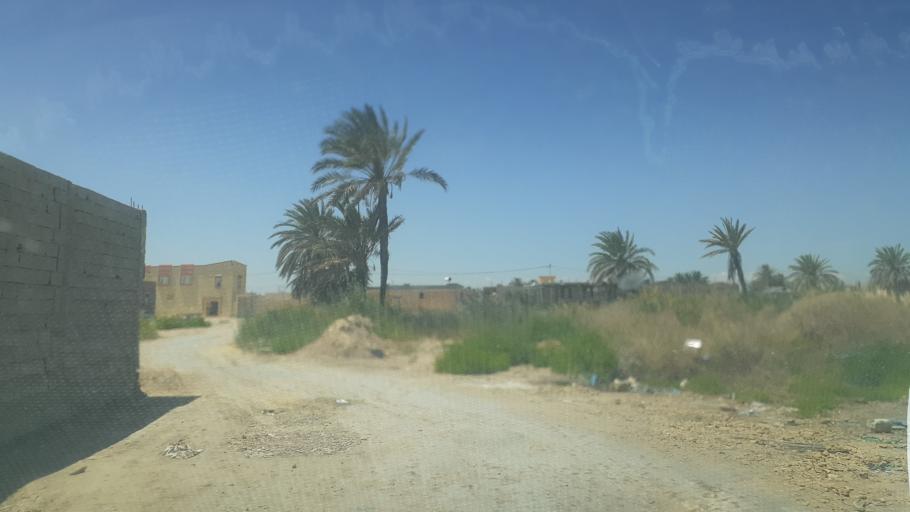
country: TN
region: Qabis
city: Gabes
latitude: 33.9348
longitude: 10.0585
